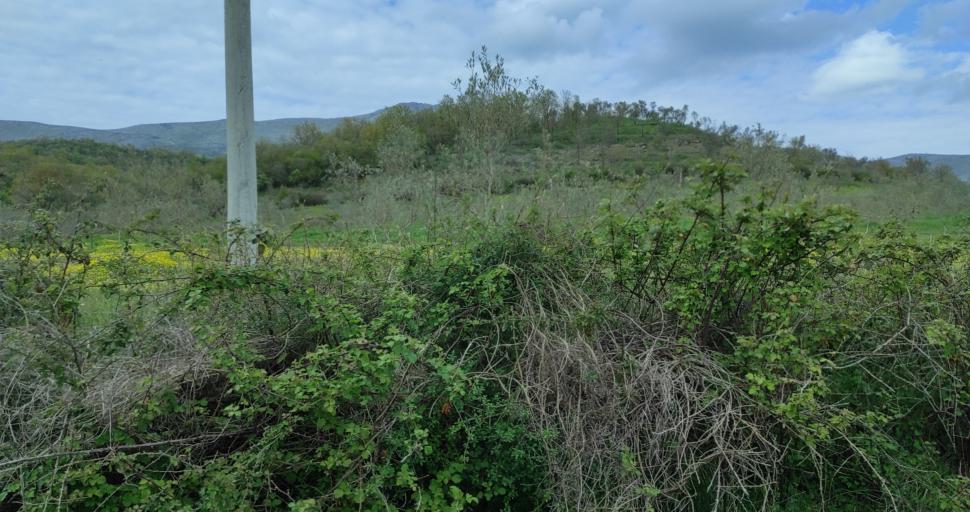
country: AL
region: Shkoder
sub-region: Rrethi i Shkodres
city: Dajc
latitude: 42.0349
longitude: 19.4047
